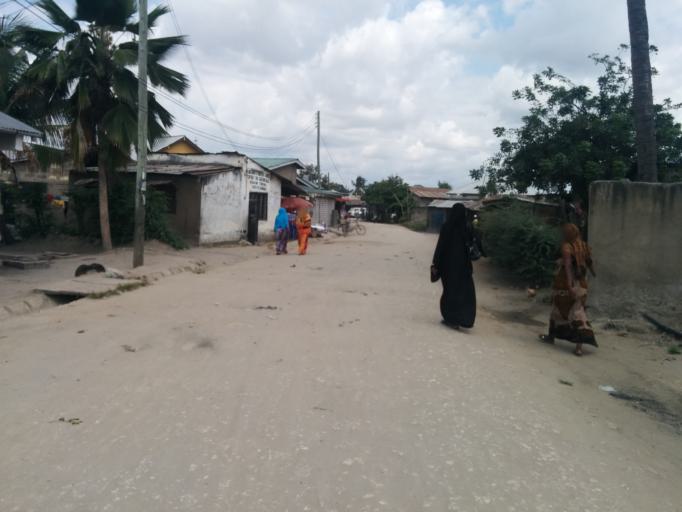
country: TZ
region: Dar es Salaam
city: Dar es Salaam
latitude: -6.8618
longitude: 39.2513
